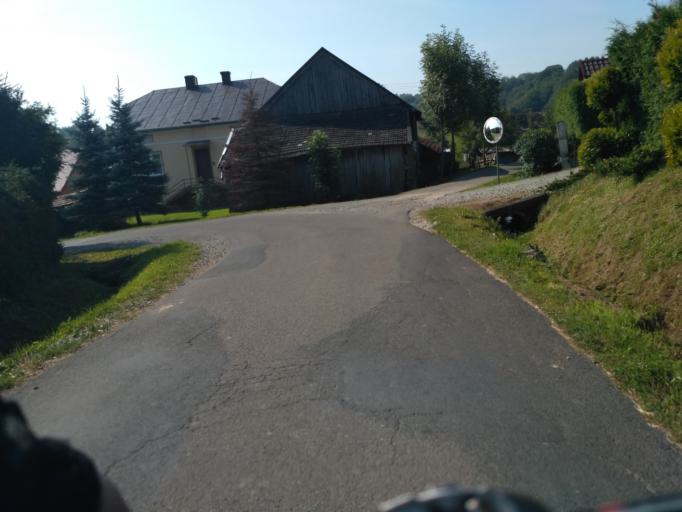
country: PL
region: Subcarpathian Voivodeship
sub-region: Powiat brzozowski
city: Golcowa
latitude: 49.7761
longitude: 22.0142
